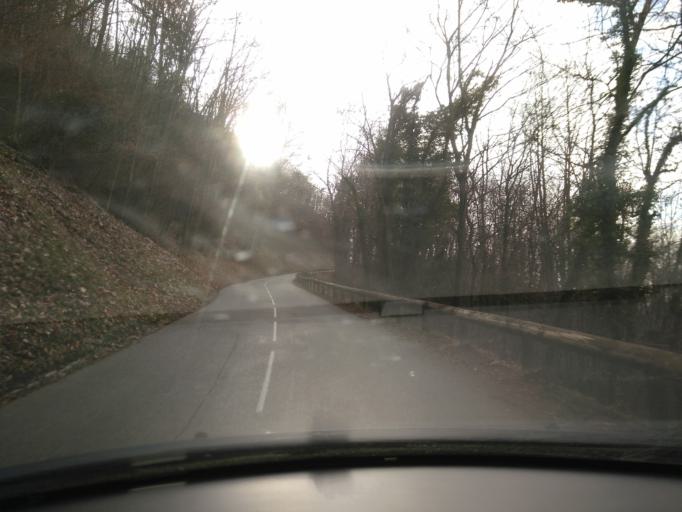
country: FR
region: Rhone-Alpes
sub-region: Departement de l'Isere
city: Villard-Bonnot
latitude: 45.2496
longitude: 5.9085
